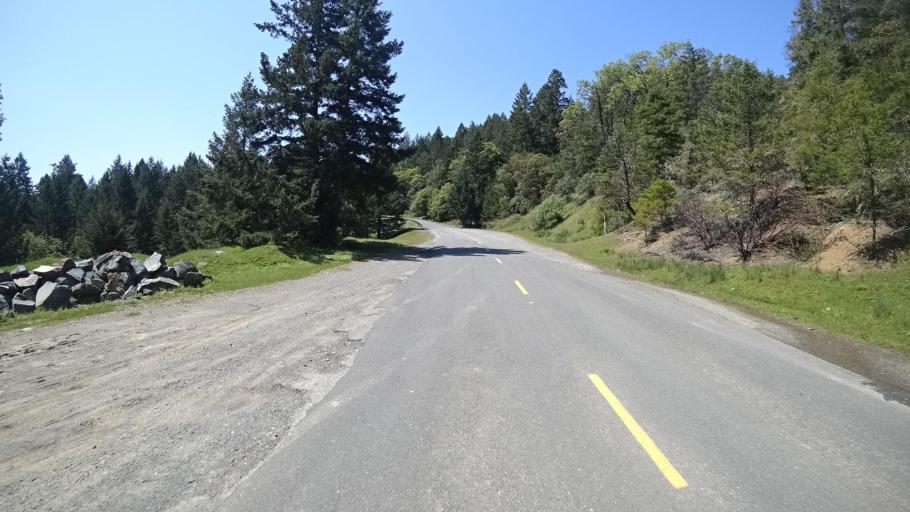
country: US
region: California
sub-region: Humboldt County
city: Redway
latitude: 40.1226
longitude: -123.6412
